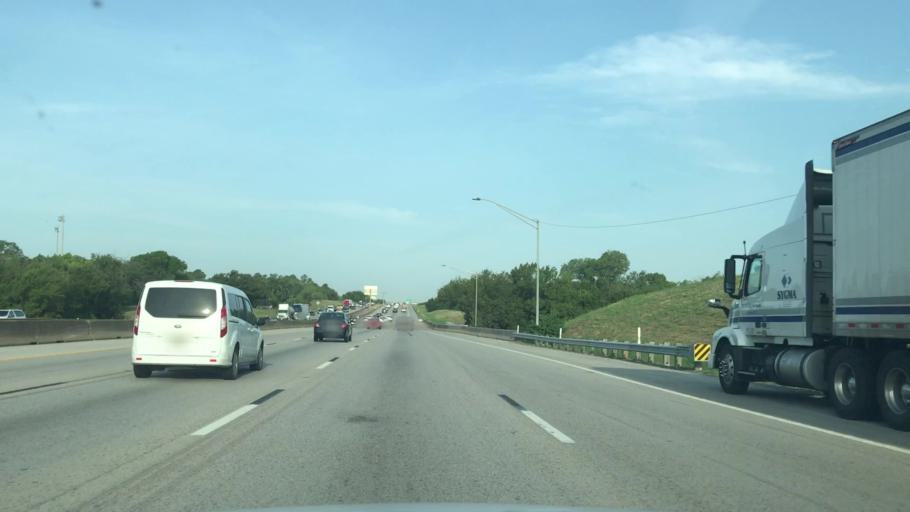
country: US
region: Texas
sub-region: Tarrant County
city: Arlington
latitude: 32.7600
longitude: -97.1350
